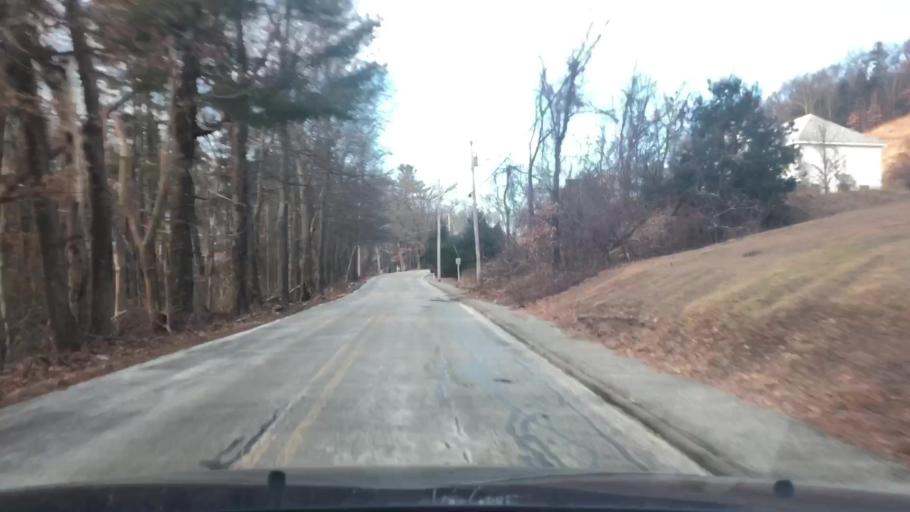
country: US
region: Massachusetts
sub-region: Essex County
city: Andover
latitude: 42.6661
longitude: -71.1088
